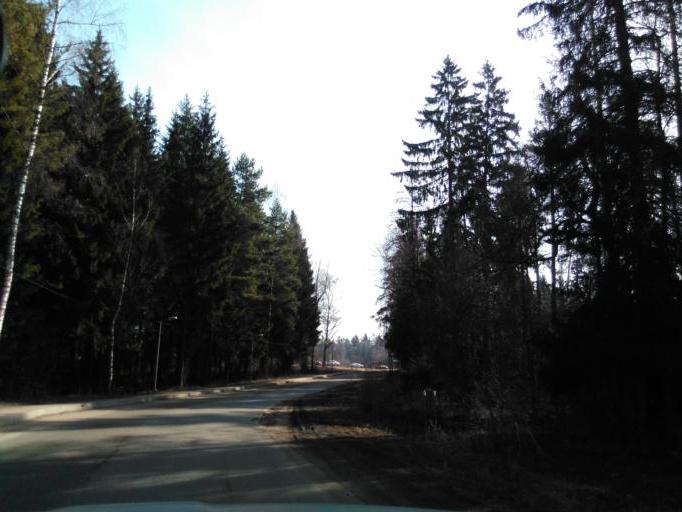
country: RU
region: Moskovskaya
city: Firsanovka
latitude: 55.9176
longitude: 37.2054
